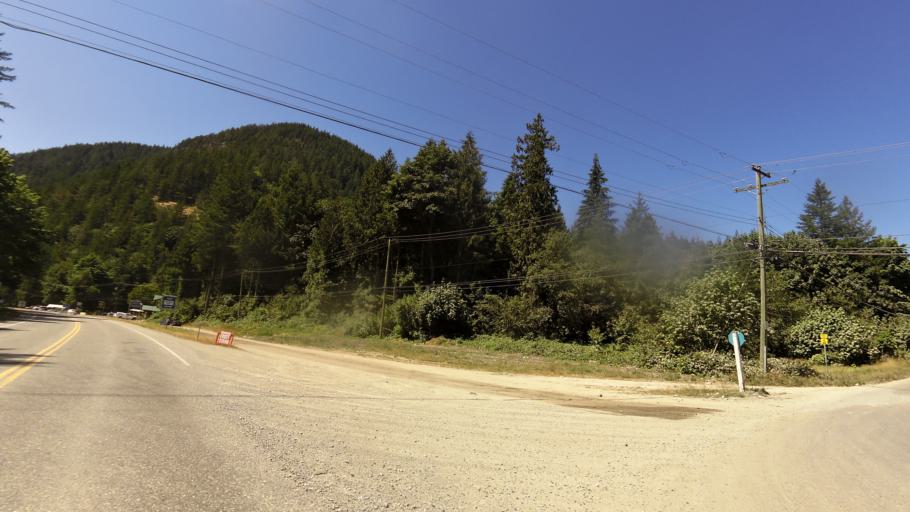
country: CA
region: British Columbia
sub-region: Fraser Valley Regional District
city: Chilliwack
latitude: 49.2513
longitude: -121.9548
